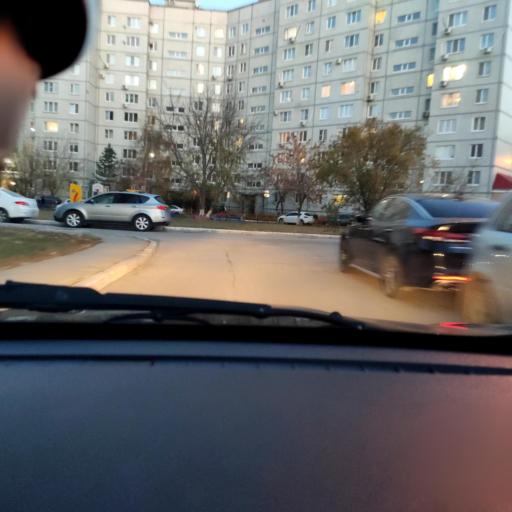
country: RU
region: Samara
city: Tol'yatti
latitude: 53.5411
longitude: 49.4006
